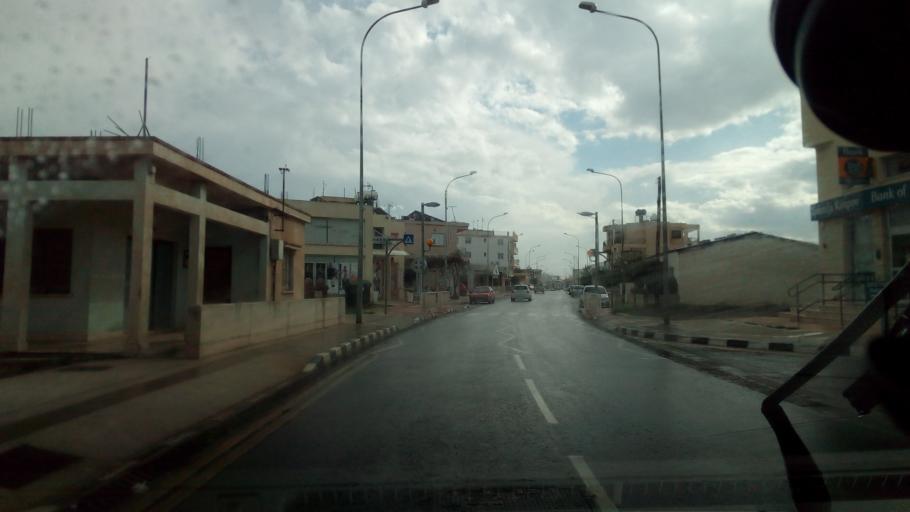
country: CY
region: Ammochostos
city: Deryneia
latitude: 35.0625
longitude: 33.9619
